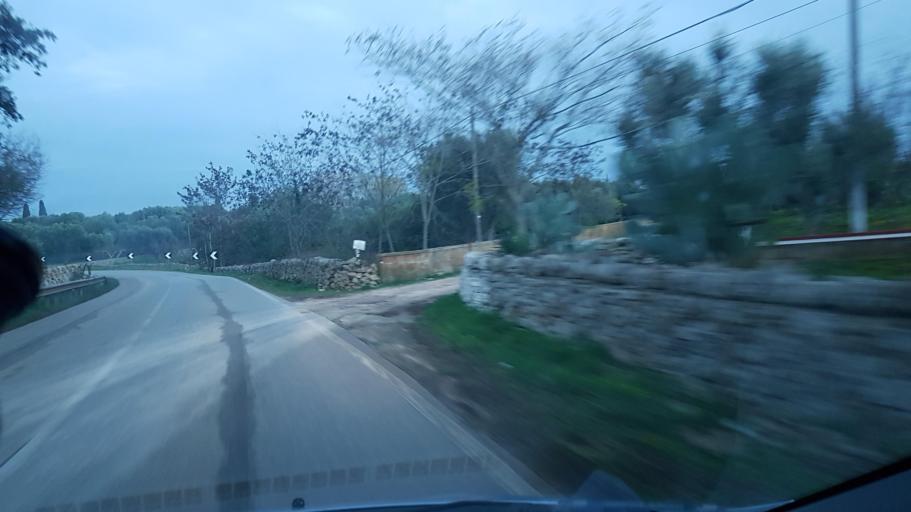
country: IT
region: Apulia
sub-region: Provincia di Brindisi
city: Ceglie Messapica
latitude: 40.6446
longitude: 17.5500
